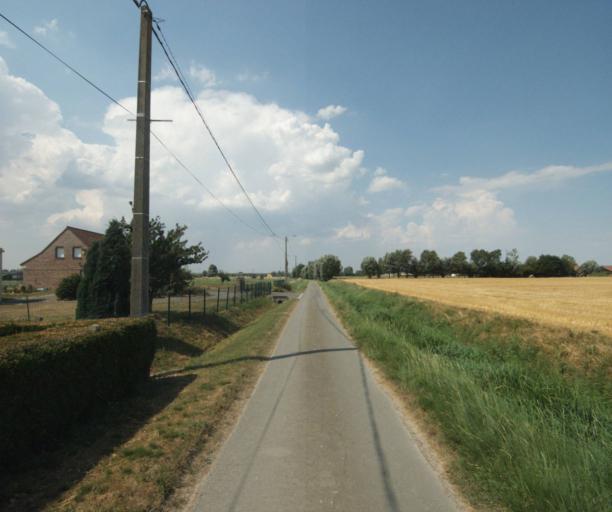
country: FR
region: Nord-Pas-de-Calais
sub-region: Departement du Nord
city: Comines
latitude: 50.7419
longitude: 2.9901
